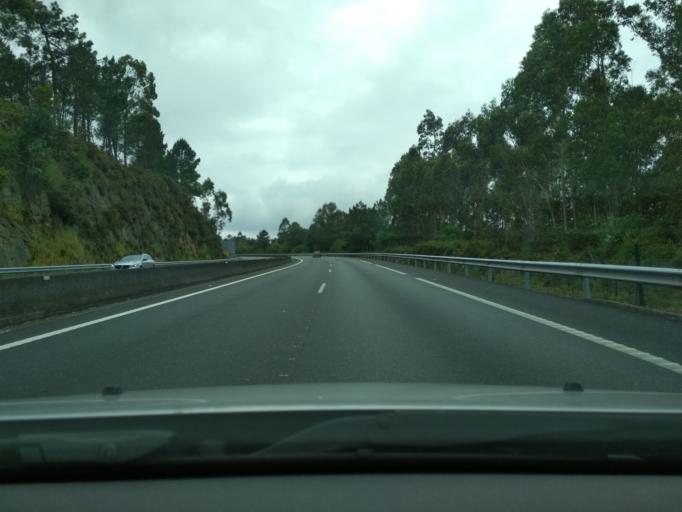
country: ES
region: Galicia
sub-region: Provincia da Coruna
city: Santiago de Compostela
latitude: 42.8469
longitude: -8.5718
